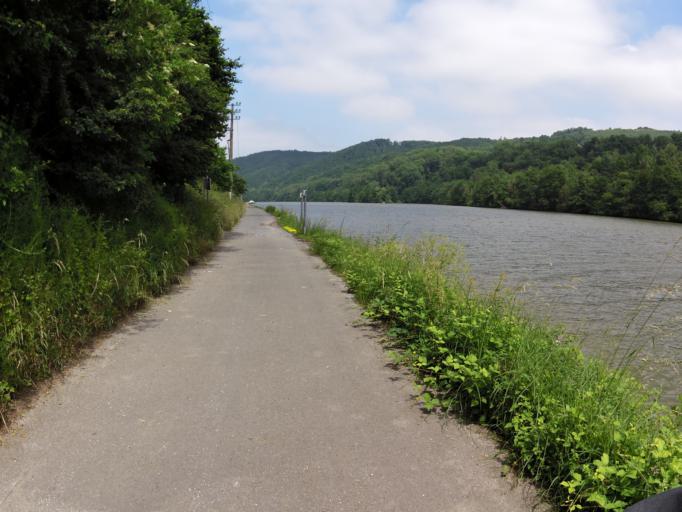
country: BE
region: Wallonia
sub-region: Province de Namur
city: Hastiere-Lavaux
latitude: 50.1850
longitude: 4.8242
